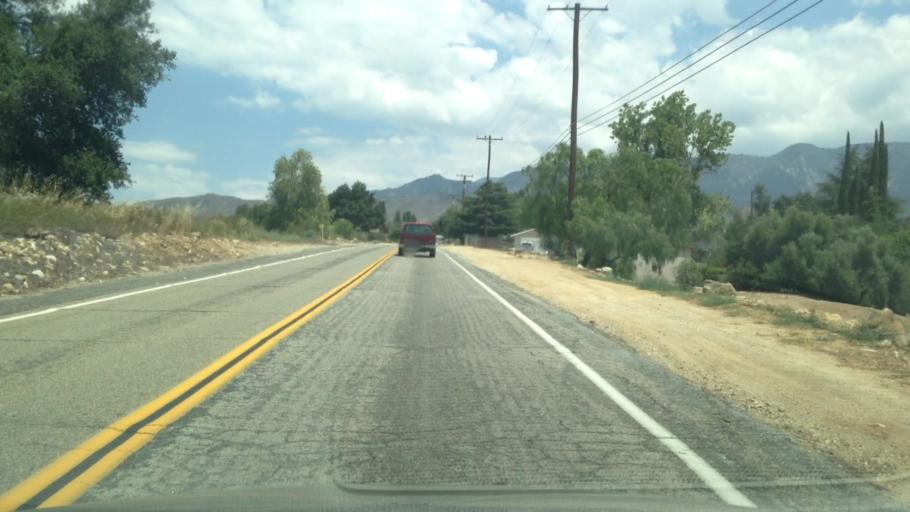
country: US
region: California
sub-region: Riverside County
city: Cherry Valley
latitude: 33.9931
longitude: -116.9635
